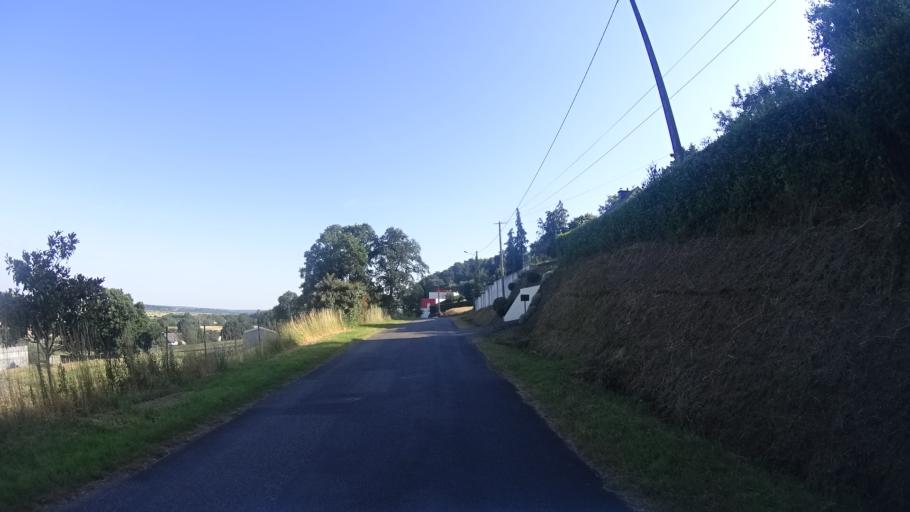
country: FR
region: Brittany
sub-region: Departement du Morbihan
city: Saint-Jean-la-Poterie
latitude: 47.6326
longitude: -2.1056
